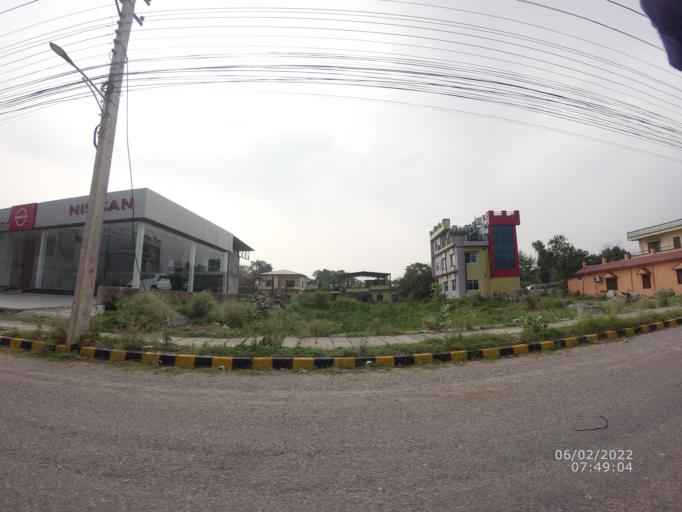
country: NP
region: Western Region
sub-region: Lumbini Zone
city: Bhairahawa
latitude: 27.5266
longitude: 83.4563
